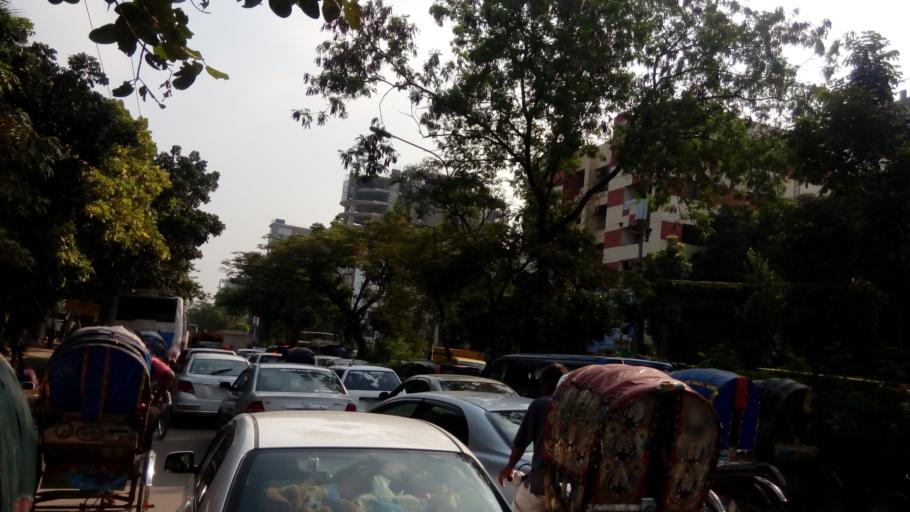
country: BD
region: Dhaka
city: Azimpur
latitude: 23.7493
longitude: 90.3694
